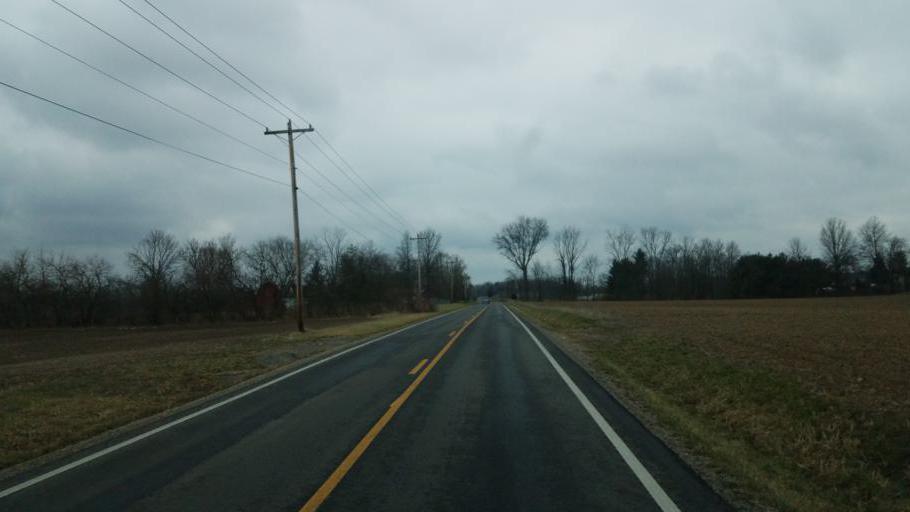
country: US
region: Ohio
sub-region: Delaware County
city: Ashley
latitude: 40.3796
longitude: -82.9433
